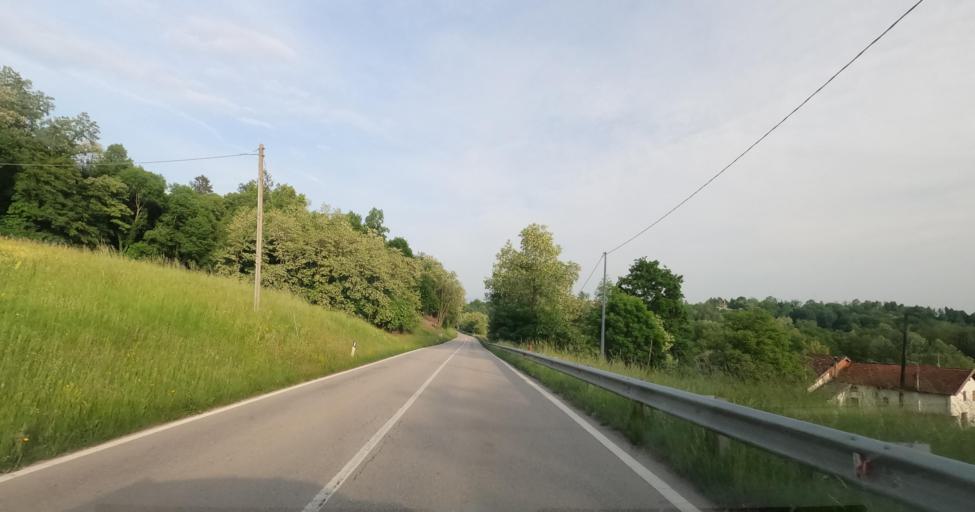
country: IT
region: Veneto
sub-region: Provincia di Belluno
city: Sedico
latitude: 46.1432
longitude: 12.1327
